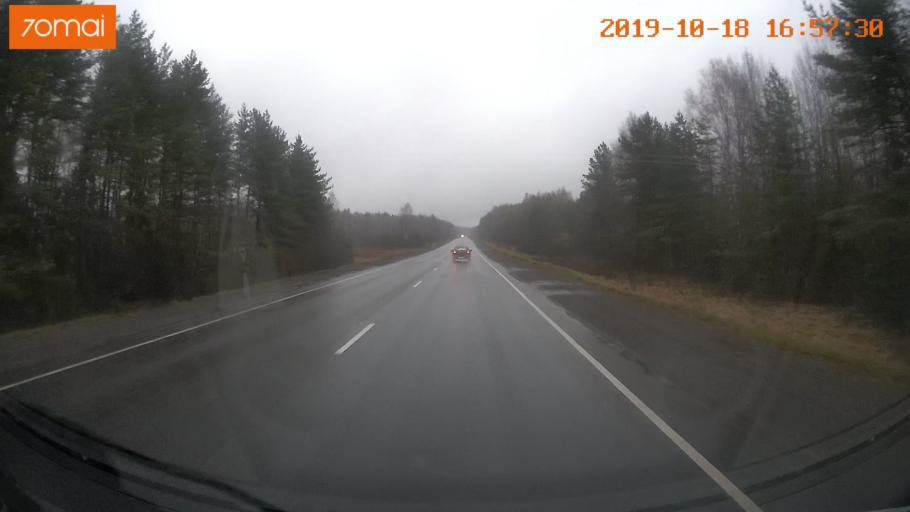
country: RU
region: Ivanovo
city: Novoye Leushino
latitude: 56.6685
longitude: 40.5959
